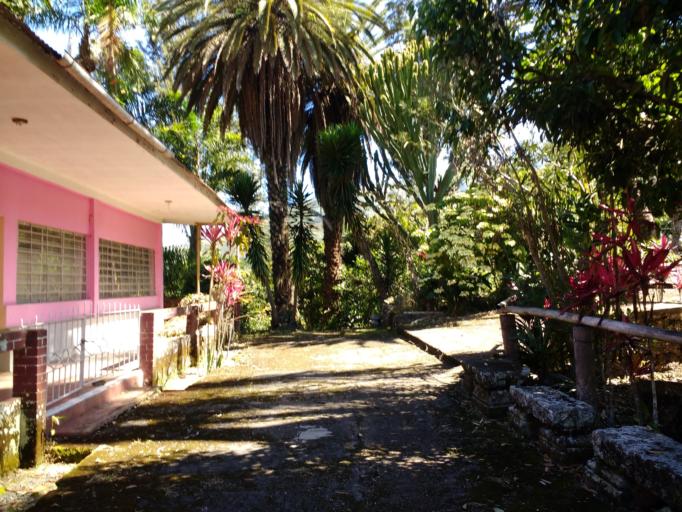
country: PE
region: Cusco
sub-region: Provincia de La Convencion
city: Maranura
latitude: -13.0043
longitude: -72.5347
